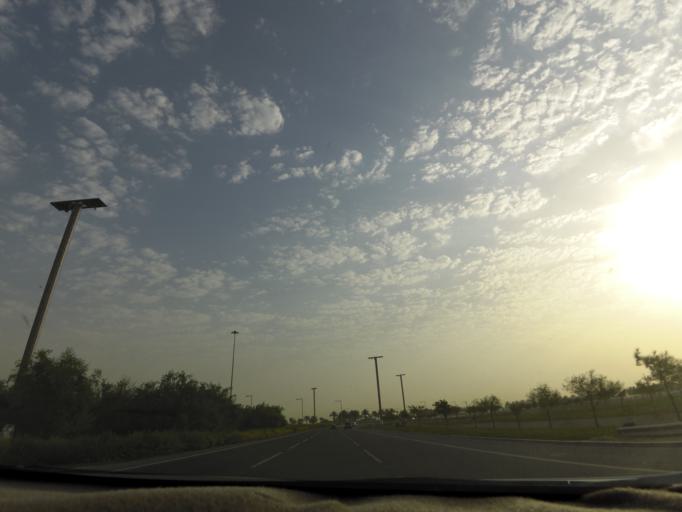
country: QA
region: Al Wakrah
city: Al Wakrah
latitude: 25.2399
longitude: 51.5944
